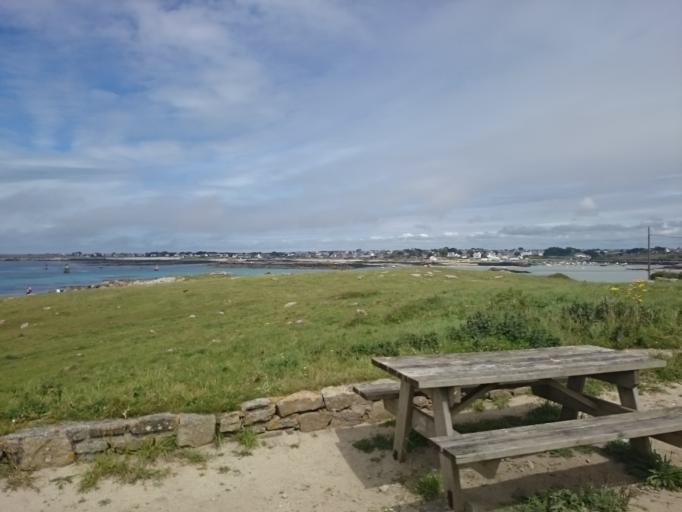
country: FR
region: Brittany
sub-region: Departement du Finistere
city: Landunvez
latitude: 48.5578
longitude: -4.7199
